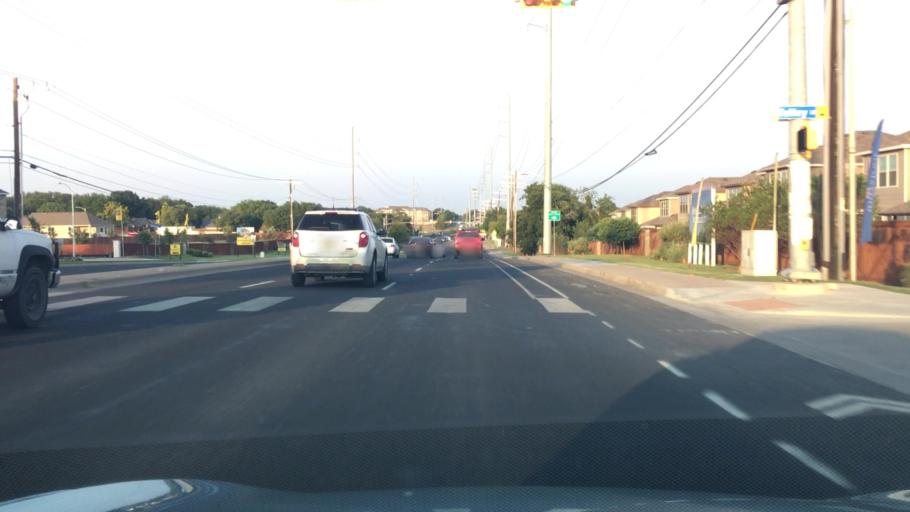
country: US
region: Texas
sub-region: Travis County
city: Manchaca
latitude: 30.1739
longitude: -97.8092
